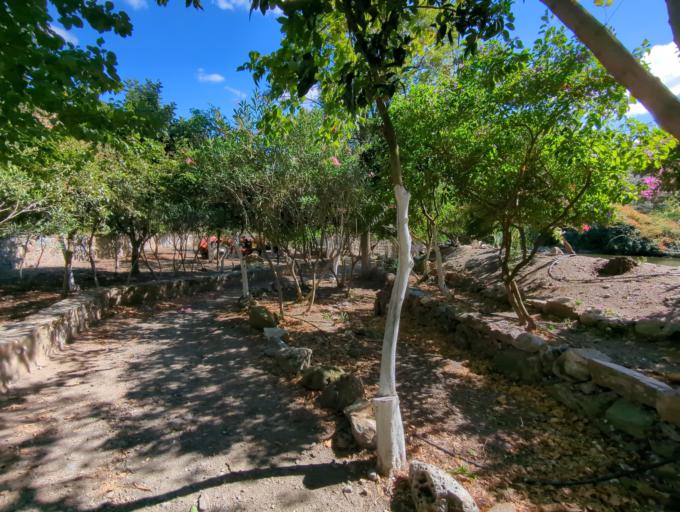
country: GR
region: Crete
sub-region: Nomos Chanias
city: Galatas
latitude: 35.4202
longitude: 23.9378
